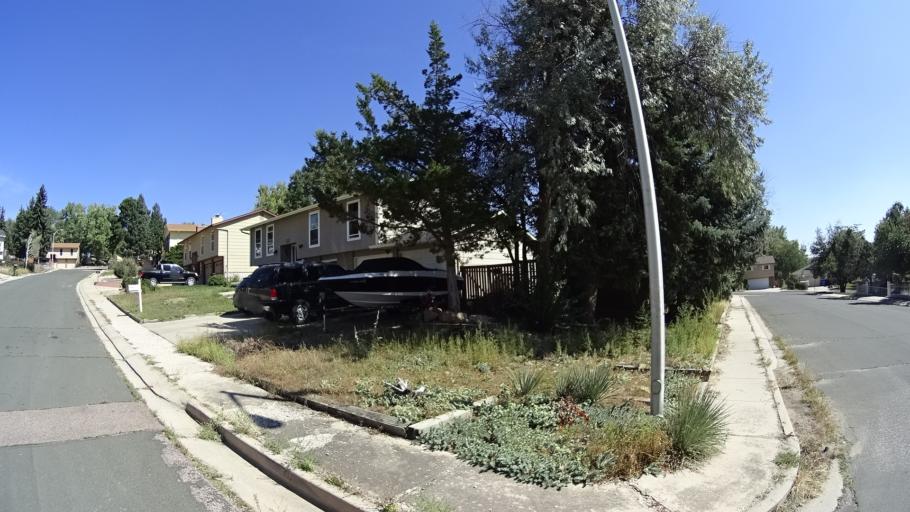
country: US
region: Colorado
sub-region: El Paso County
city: Cimarron Hills
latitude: 38.9083
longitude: -104.7662
